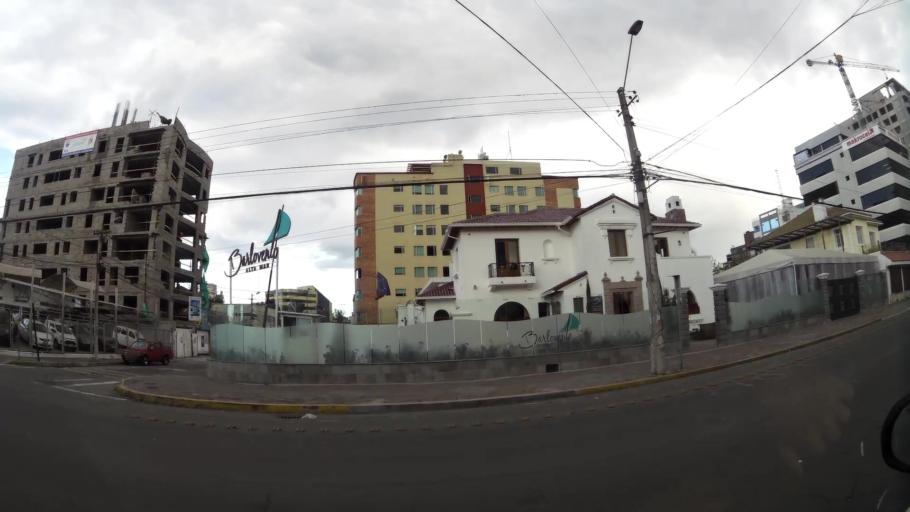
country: EC
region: Pichincha
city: Quito
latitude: -0.1987
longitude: -78.4905
